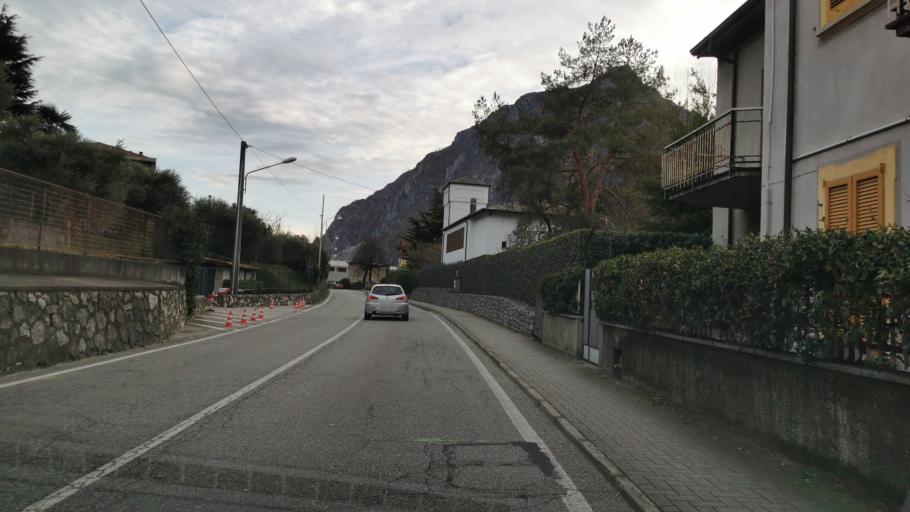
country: IT
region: Lombardy
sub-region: Provincia di Lecco
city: Abbadia Lariana
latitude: 45.8970
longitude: 9.3331
